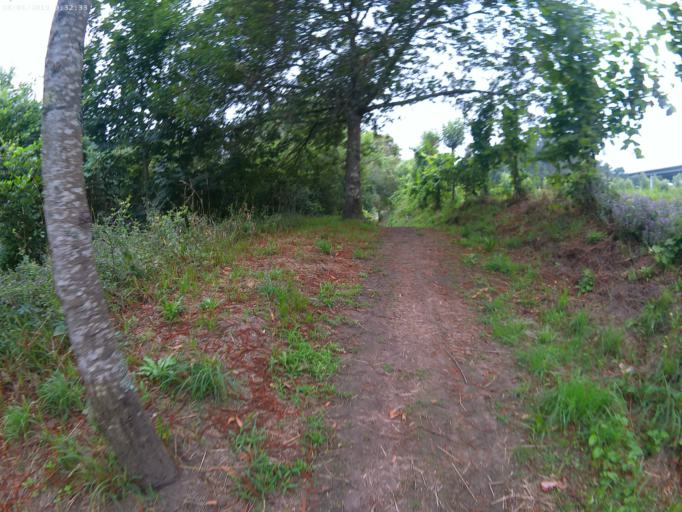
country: PT
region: Viana do Castelo
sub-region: Ponte da Barca
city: Ponte da Barca
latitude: 41.8023
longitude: -8.4717
